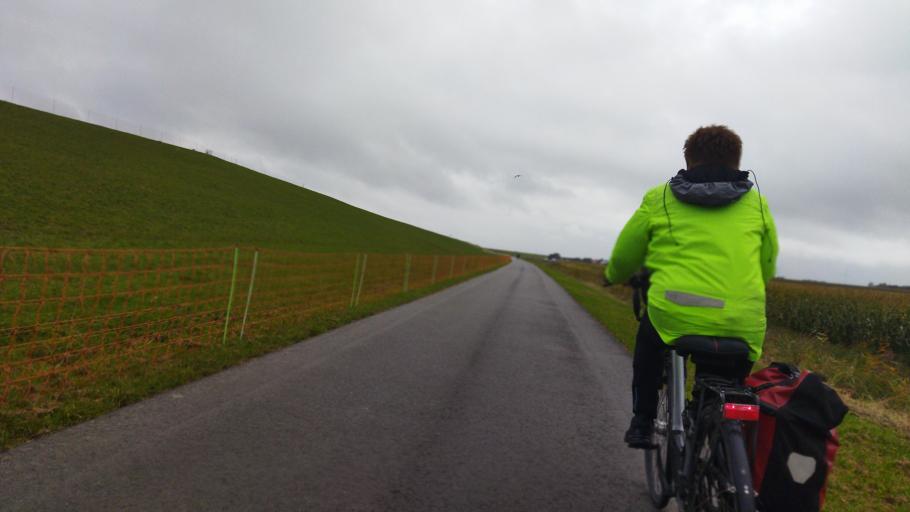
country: NL
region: Groningen
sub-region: Gemeente Delfzijl
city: Delfzijl
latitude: 53.4089
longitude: 7.0149
